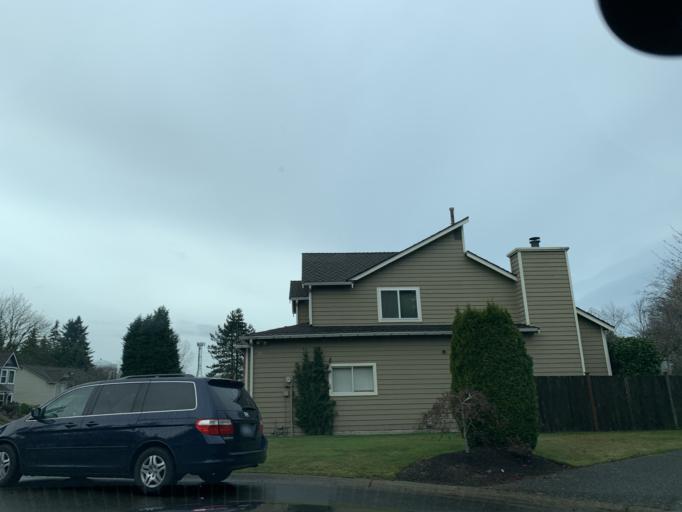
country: US
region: Washington
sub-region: King County
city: Woodinville
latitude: 47.7441
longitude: -122.1705
